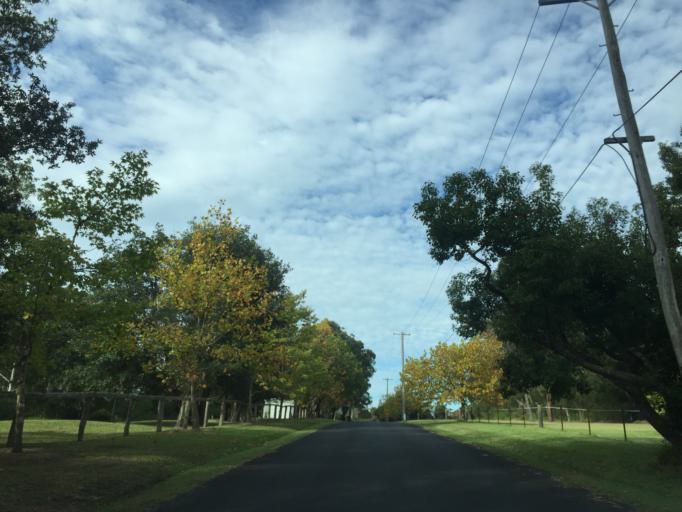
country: AU
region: New South Wales
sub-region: Hornsby Shire
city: Galston
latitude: -33.6454
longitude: 151.0767
